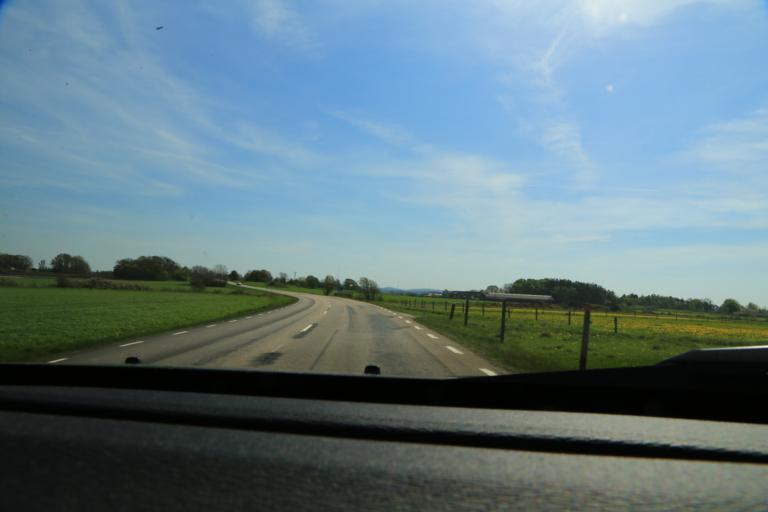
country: SE
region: Halland
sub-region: Varbergs Kommun
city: Varberg
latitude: 57.1366
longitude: 12.3017
